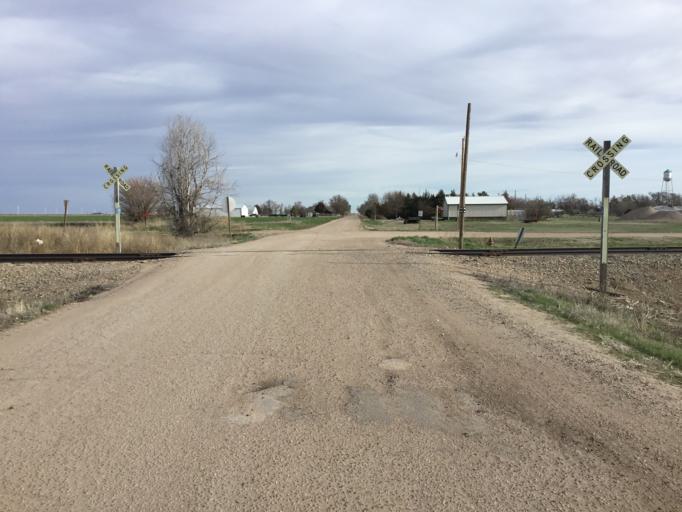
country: US
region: Colorado
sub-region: Kit Carson County
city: Burlington
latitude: 39.3325
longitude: -102.0421
